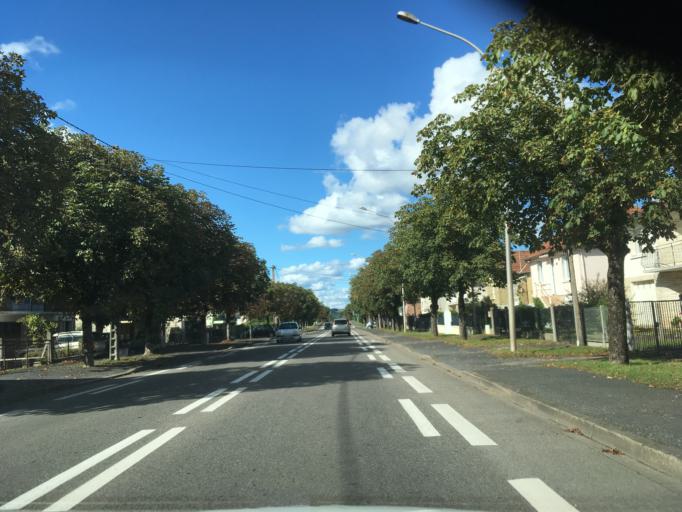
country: FR
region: Limousin
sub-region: Departement de la Correze
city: Brive-la-Gaillarde
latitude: 45.1441
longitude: 1.4908
